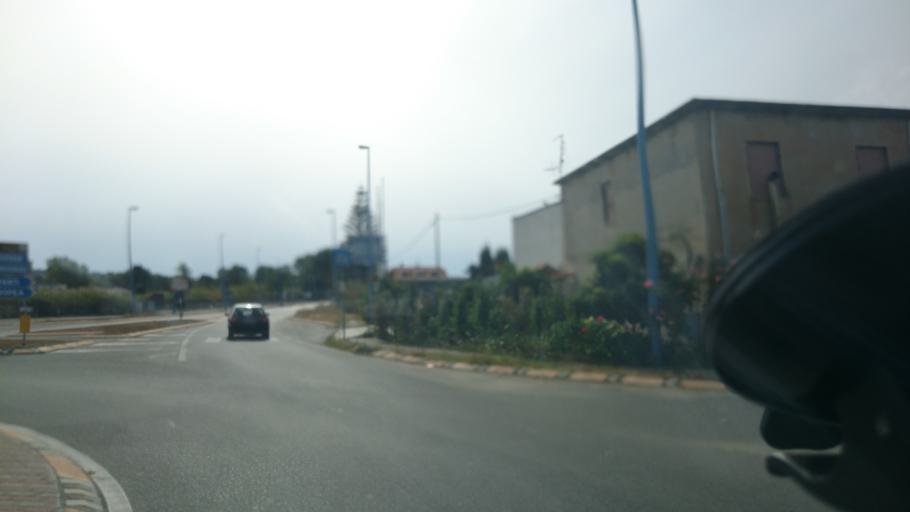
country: IT
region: Calabria
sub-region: Provincia di Vibo-Valentia
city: Vibo Valentia
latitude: 38.7111
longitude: 16.0860
